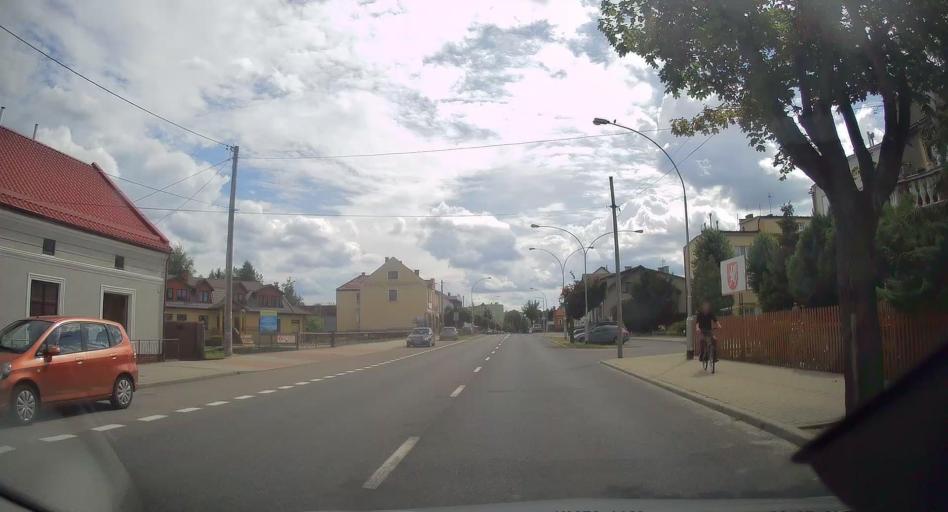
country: PL
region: Subcarpathian Voivodeship
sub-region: Powiat debicki
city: Debica
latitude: 50.0469
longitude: 21.4048
